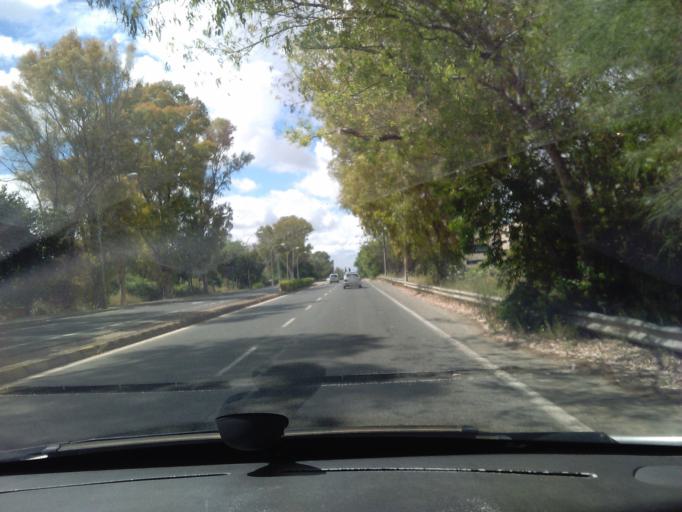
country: ES
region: Andalusia
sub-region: Provincia de Sevilla
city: Sevilla
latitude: 37.3519
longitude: -5.9773
